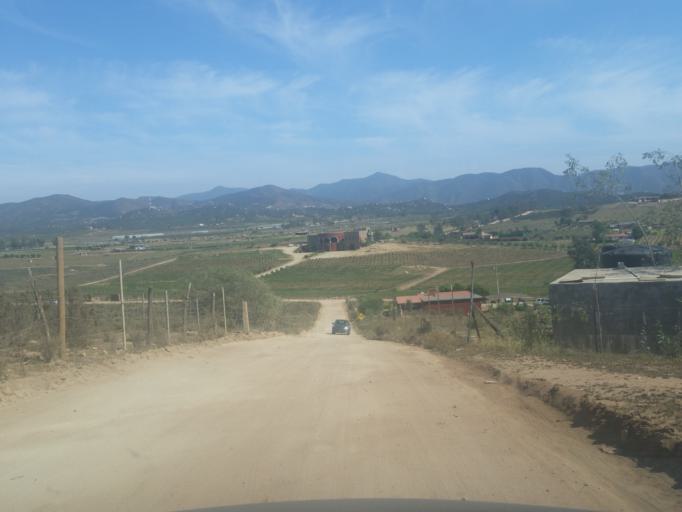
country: MX
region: Baja California
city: El Sauzal
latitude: 32.0193
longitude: -116.6674
